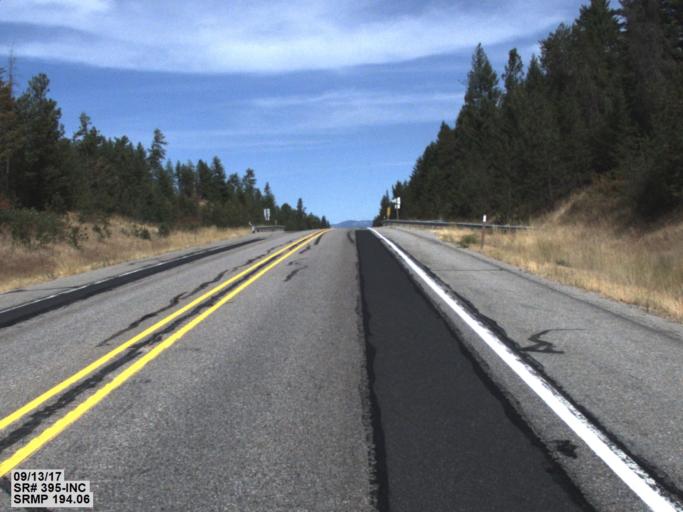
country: US
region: Washington
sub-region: Stevens County
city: Chewelah
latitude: 48.1081
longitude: -117.6432
